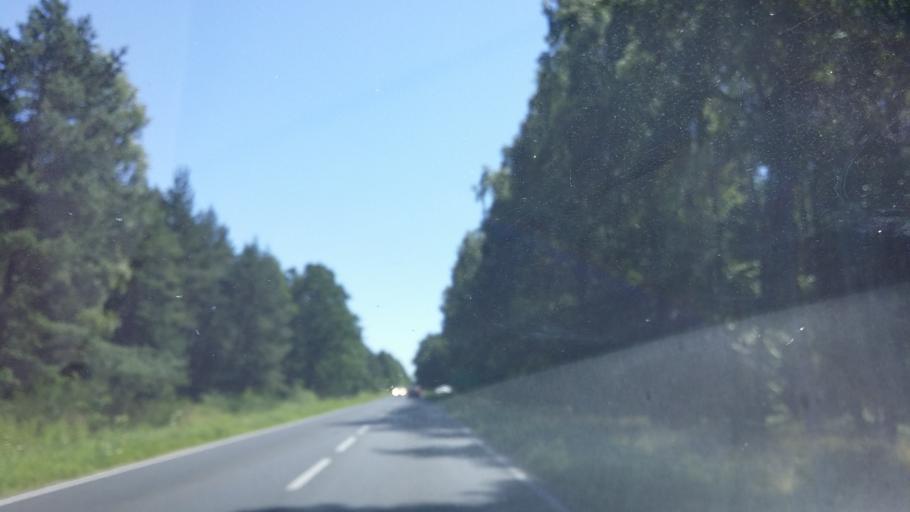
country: PL
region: West Pomeranian Voivodeship
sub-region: Powiat kolobrzeski
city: Kolobrzeg
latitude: 54.1193
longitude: 15.5859
